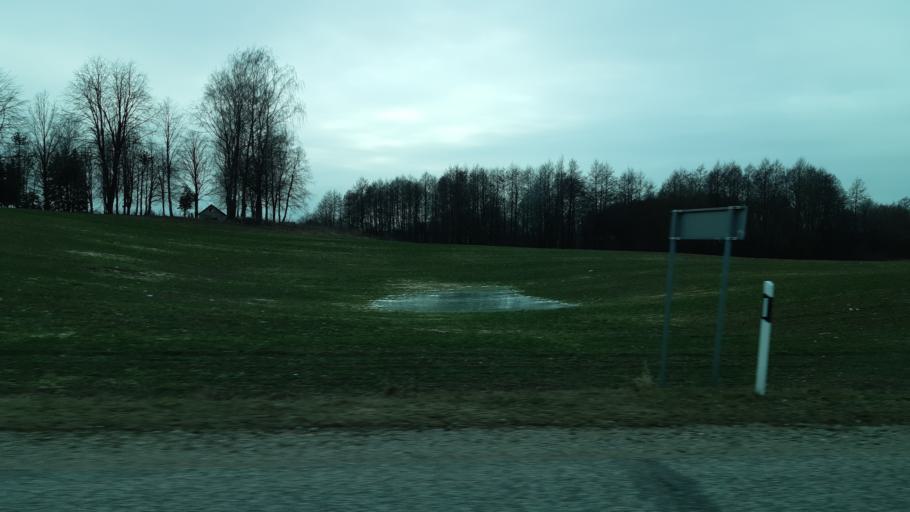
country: LT
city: Kybartai
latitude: 54.5382
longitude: 22.7185
